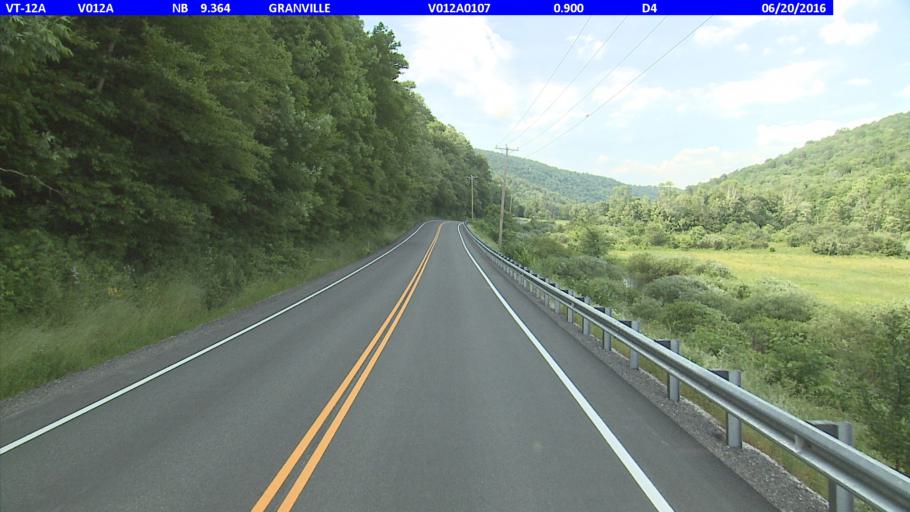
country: US
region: Vermont
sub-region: Orange County
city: Randolph
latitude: 44.0229
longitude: -72.7601
